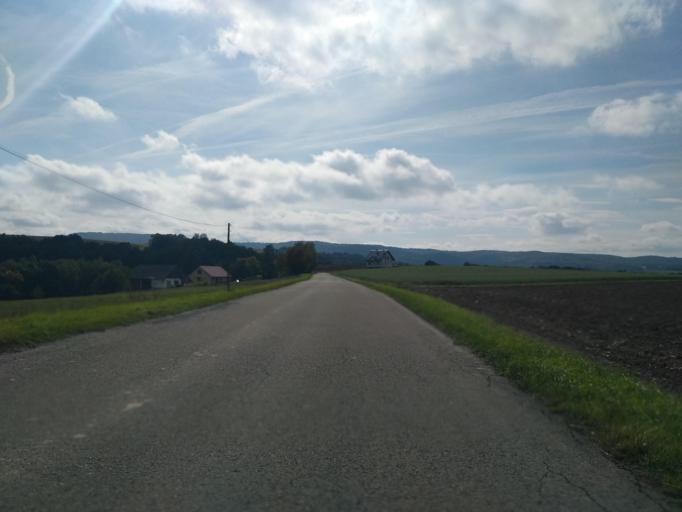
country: PL
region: Subcarpathian Voivodeship
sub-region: Powiat ropczycko-sedziszowski
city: Wielopole Skrzynskie
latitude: 49.9241
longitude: 21.5651
